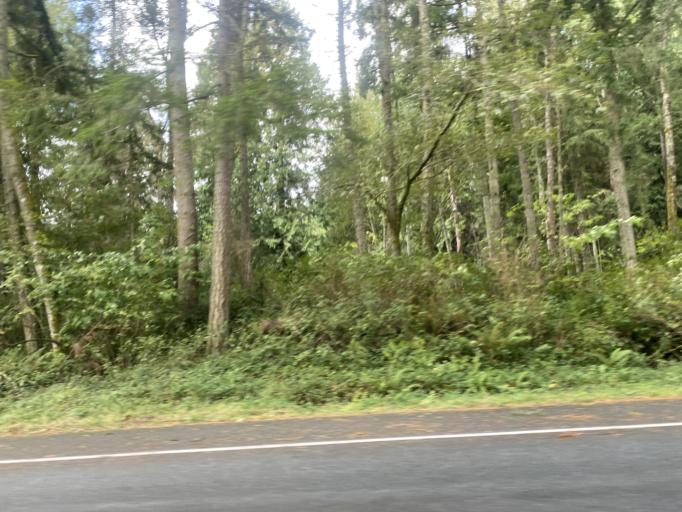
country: US
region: Washington
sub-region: Island County
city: Langley
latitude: 48.0177
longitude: -122.4095
